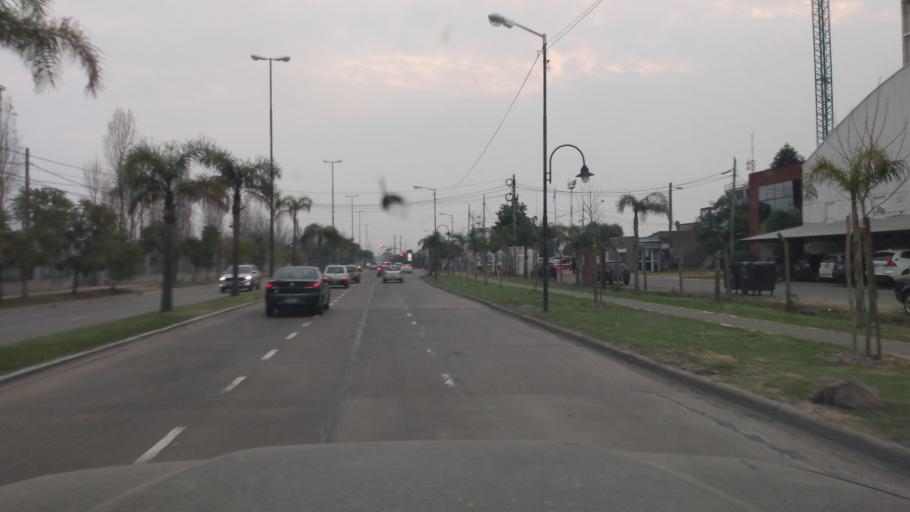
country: AR
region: Buenos Aires
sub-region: Partido de Tigre
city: Tigre
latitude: -34.4559
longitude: -58.5825
